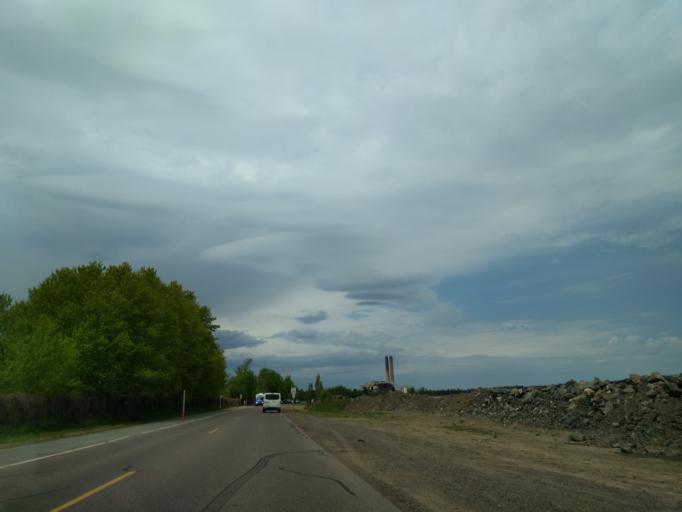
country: US
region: Michigan
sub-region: Marquette County
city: Marquette
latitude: 46.5651
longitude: -87.3904
